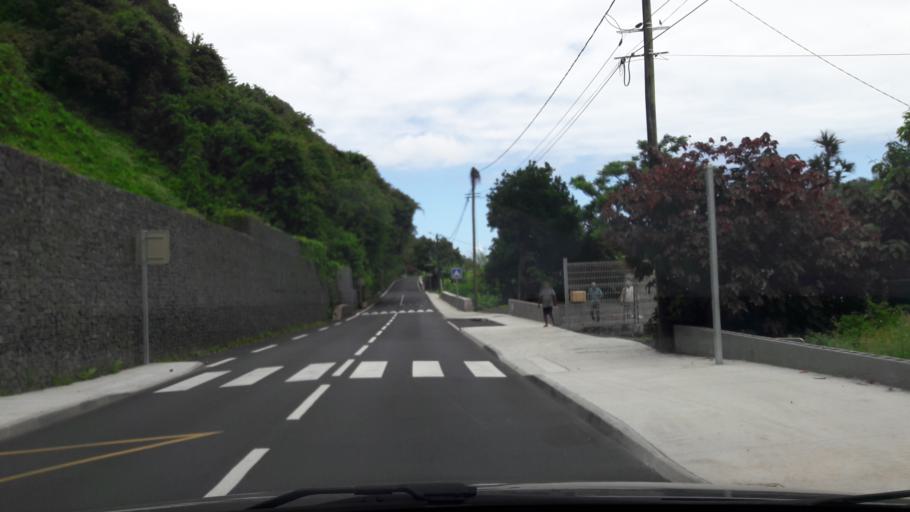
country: RE
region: Reunion
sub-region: Reunion
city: Saint-Andre
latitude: -20.9887
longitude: 55.6168
